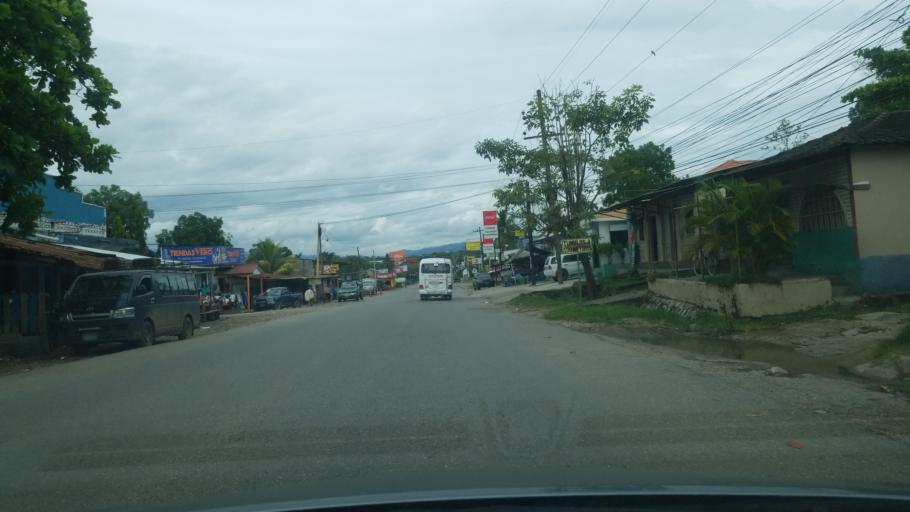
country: HN
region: Santa Barbara
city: El Ciruelo
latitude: 15.2940
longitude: -88.4899
